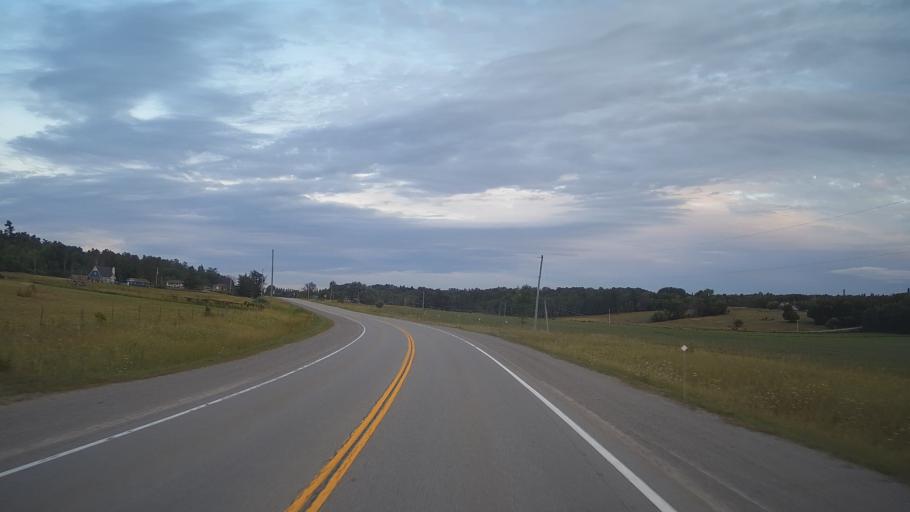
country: CA
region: Ontario
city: Pembroke
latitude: 45.7263
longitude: -76.9961
